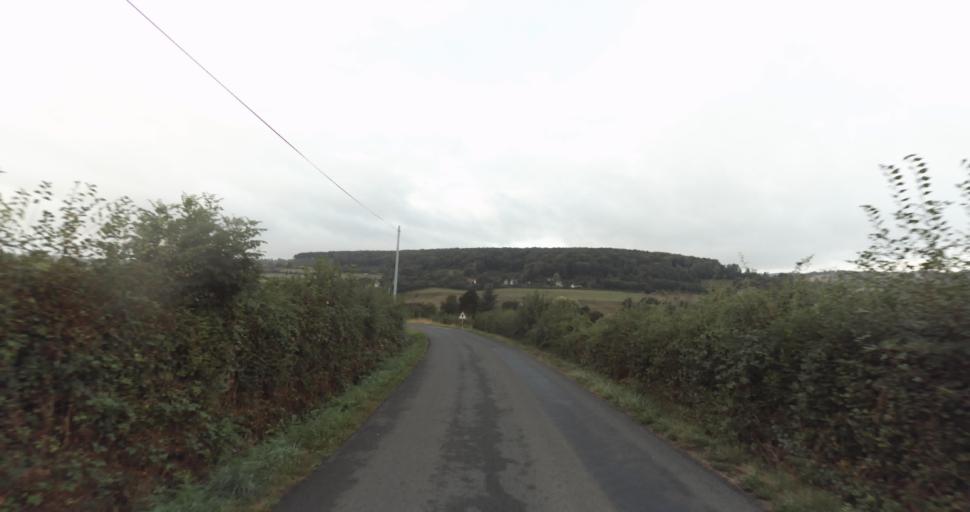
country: FR
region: Lower Normandy
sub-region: Departement de l'Orne
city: Vimoutiers
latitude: 48.9120
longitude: 0.2156
